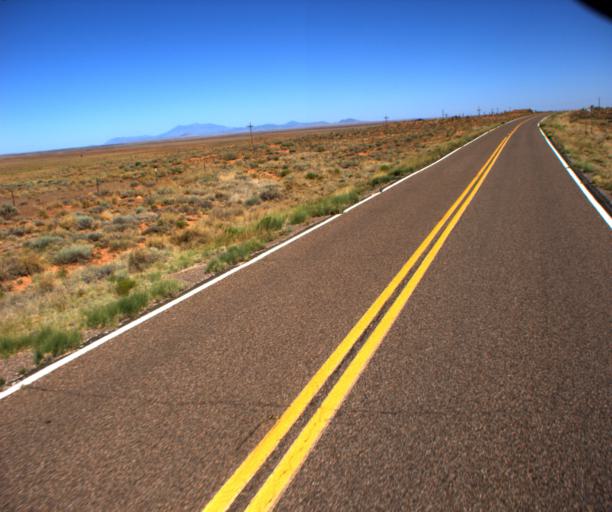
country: US
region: Arizona
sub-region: Coconino County
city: LeChee
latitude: 35.1119
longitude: -110.8688
